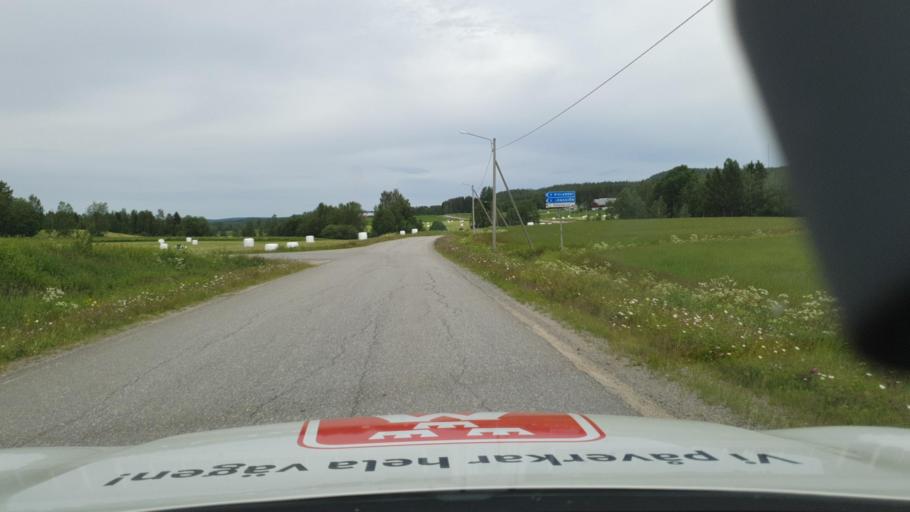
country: SE
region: Vaesterbotten
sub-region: Robertsfors Kommun
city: Robertsfors
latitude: 64.2548
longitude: 20.6563
